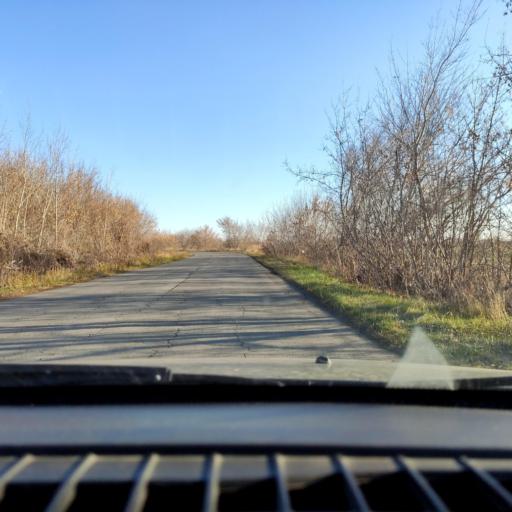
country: RU
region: Samara
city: Tol'yatti
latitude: 53.6327
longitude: 49.3038
